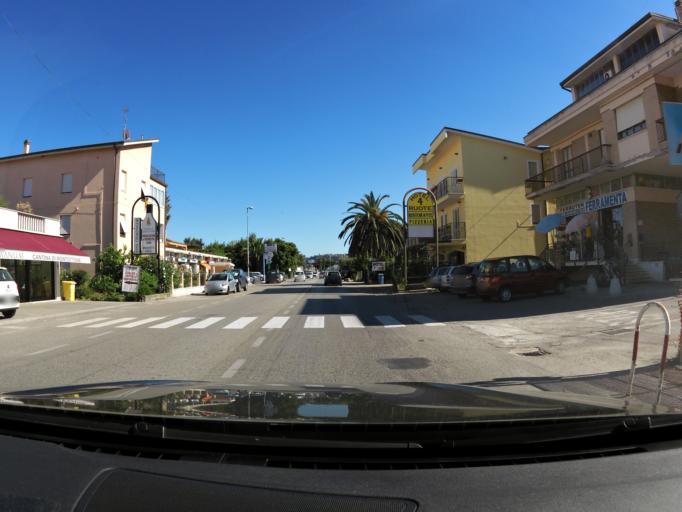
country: IT
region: The Marches
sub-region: Province of Fermo
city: Porto San Giorgio
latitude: 43.1669
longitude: 13.7996
